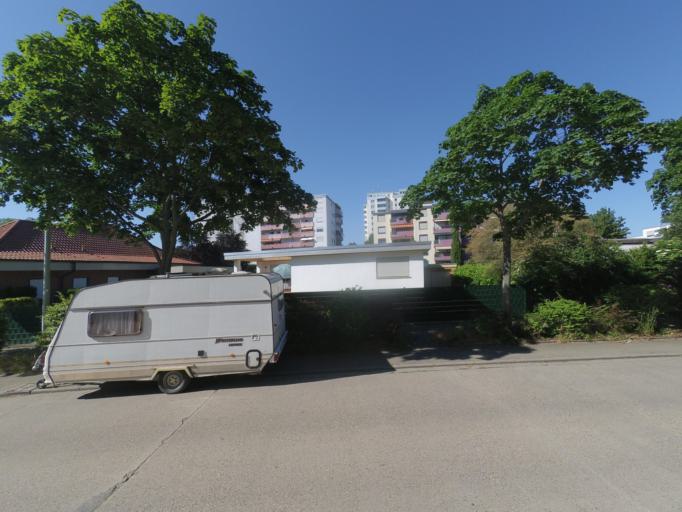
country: DE
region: Hesse
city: Lampertheim
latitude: 49.5923
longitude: 8.4568
